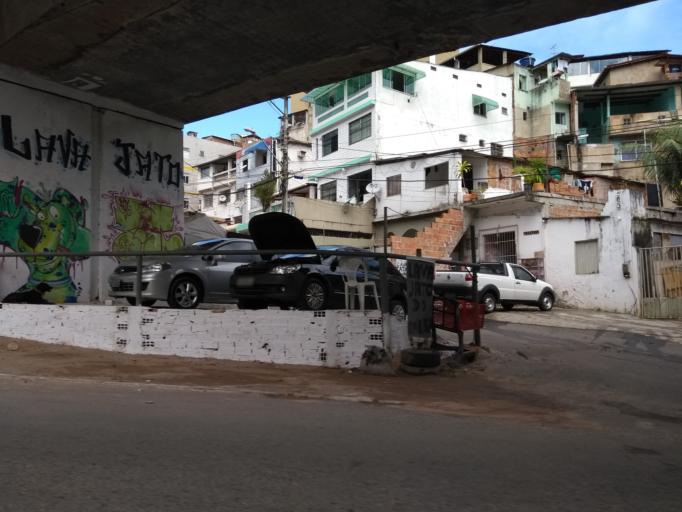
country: BR
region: Bahia
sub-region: Salvador
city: Salvador
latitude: -12.9908
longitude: -38.5233
